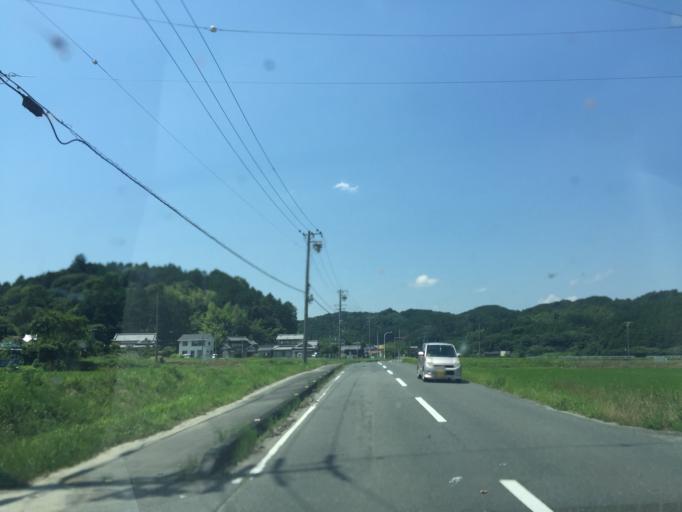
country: JP
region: Shizuoka
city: Mori
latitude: 34.8034
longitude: 137.9752
